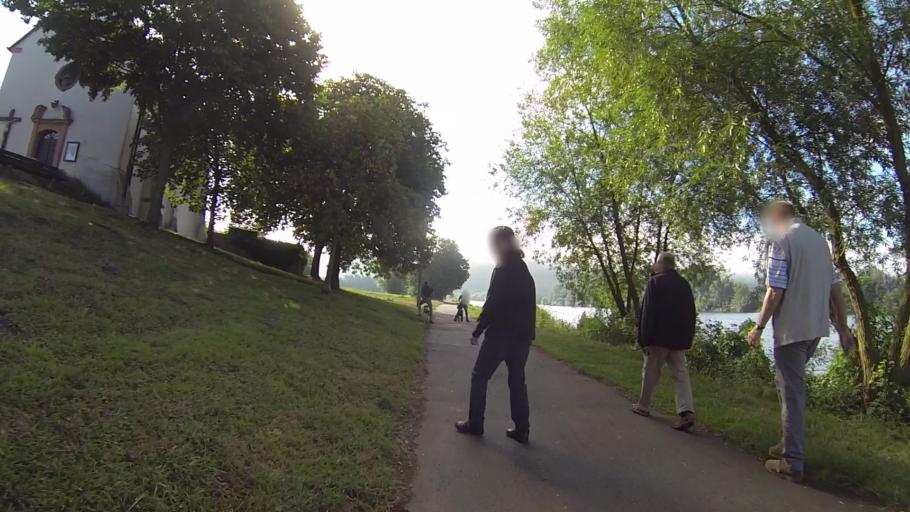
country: DE
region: Rheinland-Pfalz
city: Schweich
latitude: 49.8168
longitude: 6.7365
